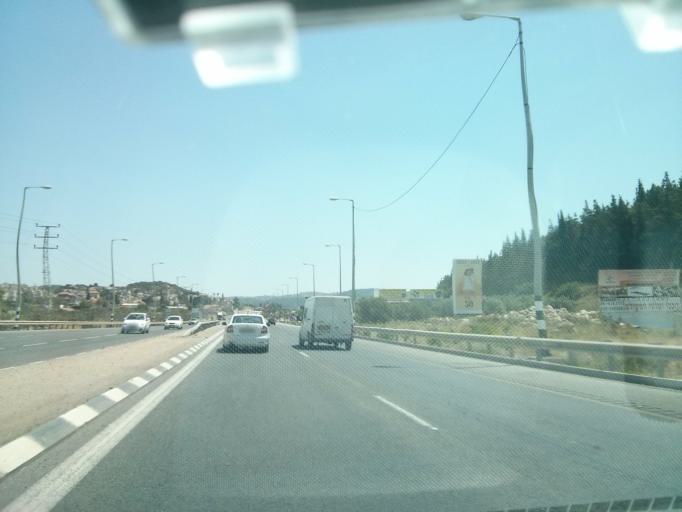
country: PS
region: West Bank
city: Barta`ah ash Sharqiyah
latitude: 32.5003
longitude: 35.0695
